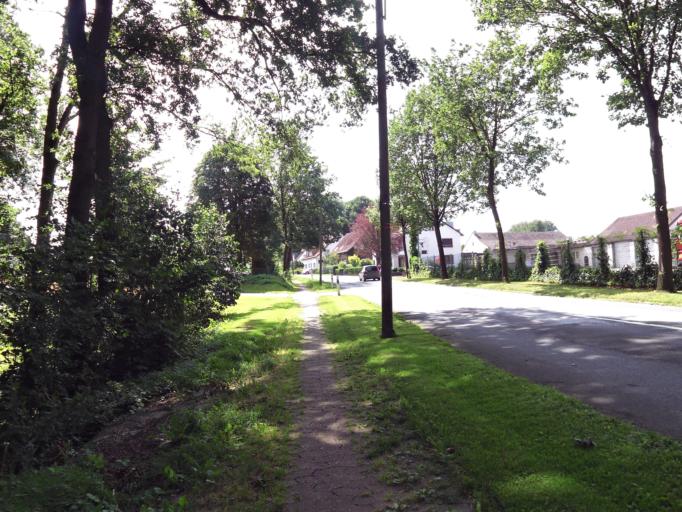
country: DE
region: North Rhine-Westphalia
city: Spenge
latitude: 52.1324
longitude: 8.4673
